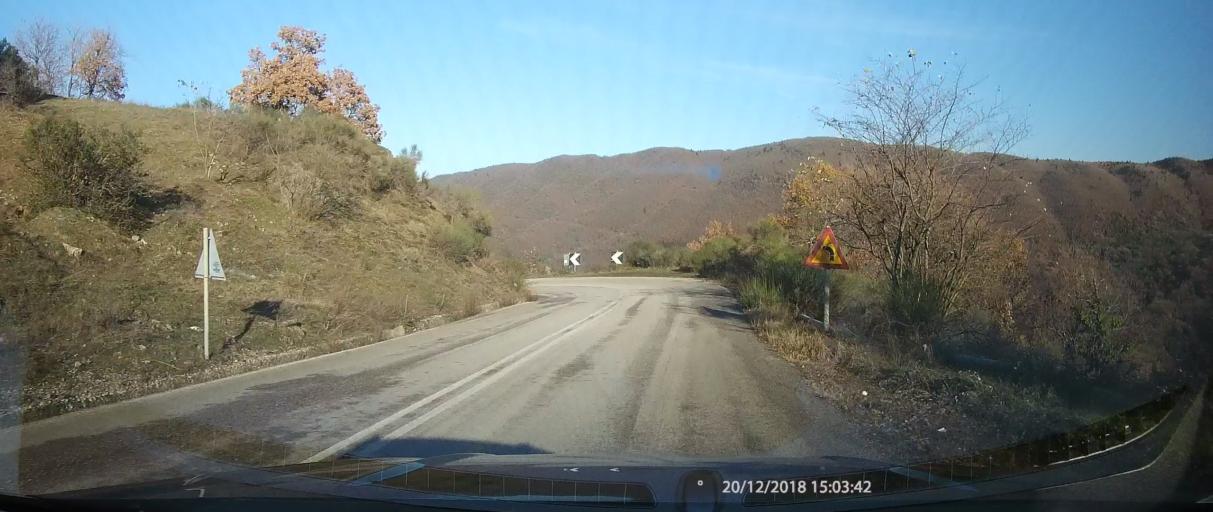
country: GR
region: Central Greece
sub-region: Nomos Evrytanias
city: Karpenisi
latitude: 38.9115
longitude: 21.9239
